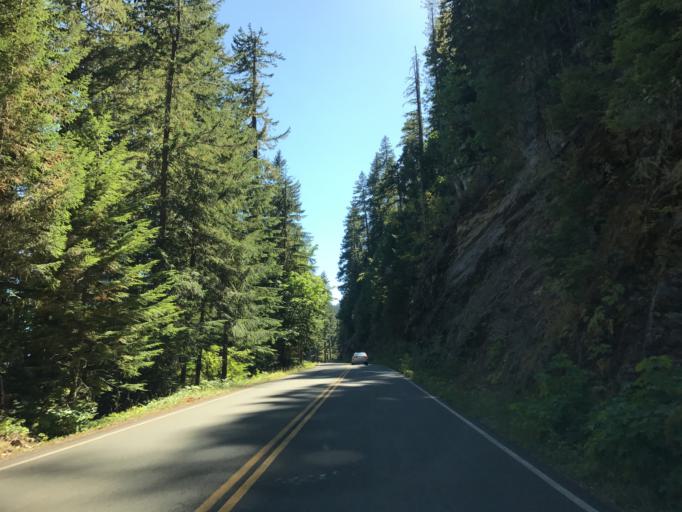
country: US
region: Washington
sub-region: Pierce County
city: Buckley
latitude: 46.7321
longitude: -121.5824
